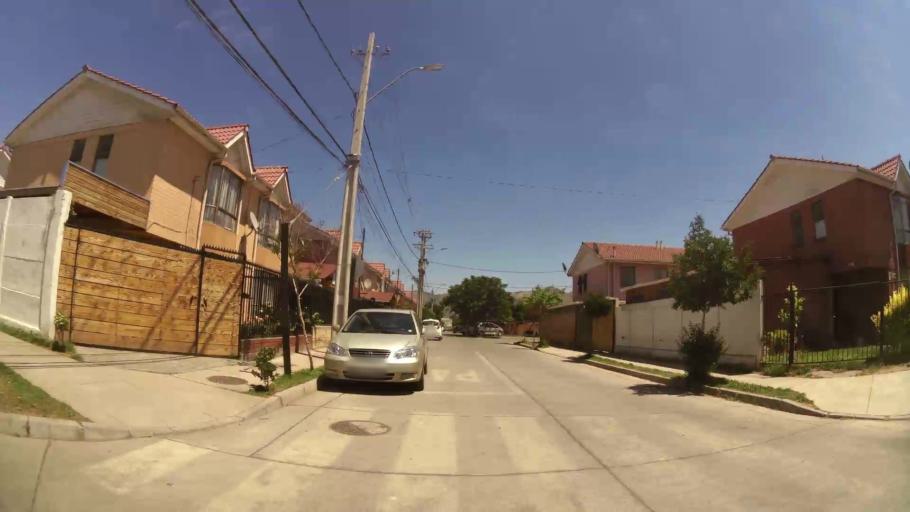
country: CL
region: Santiago Metropolitan
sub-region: Provincia de Maipo
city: San Bernardo
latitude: -33.6164
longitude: -70.7073
